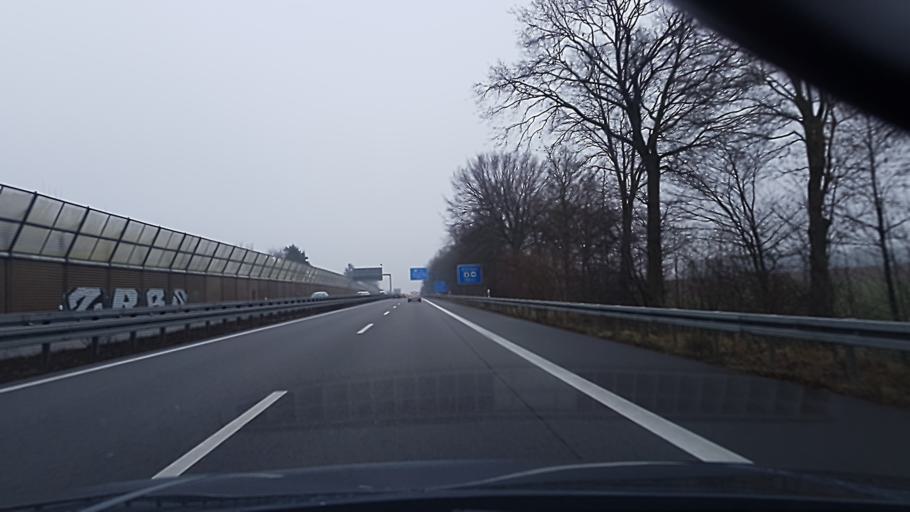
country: DE
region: Lower Saxony
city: Leiferde
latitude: 52.2216
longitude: 10.4983
